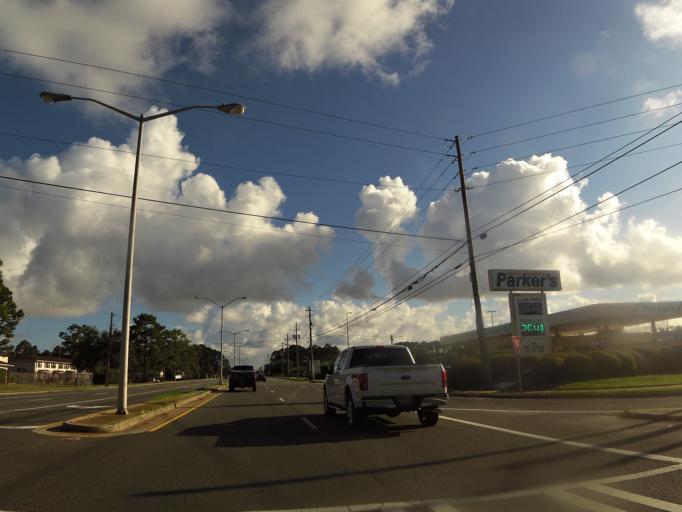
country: US
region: Georgia
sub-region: Glynn County
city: Country Club Estates
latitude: 31.2147
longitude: -81.4804
